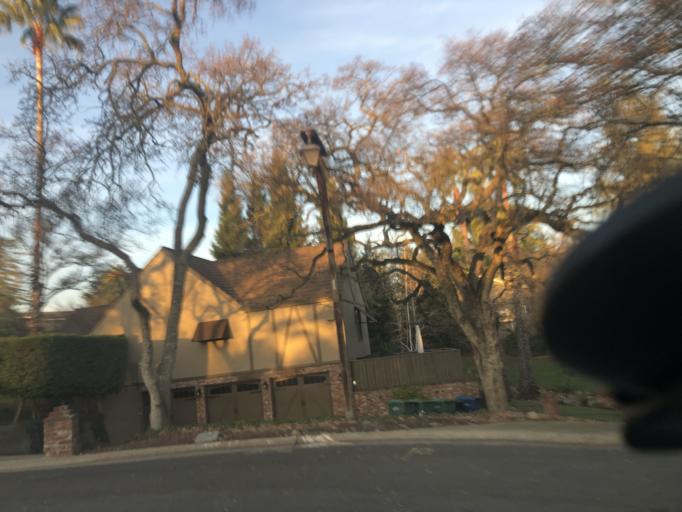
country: US
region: California
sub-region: Sacramento County
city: Gold River
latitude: 38.6398
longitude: -121.2317
